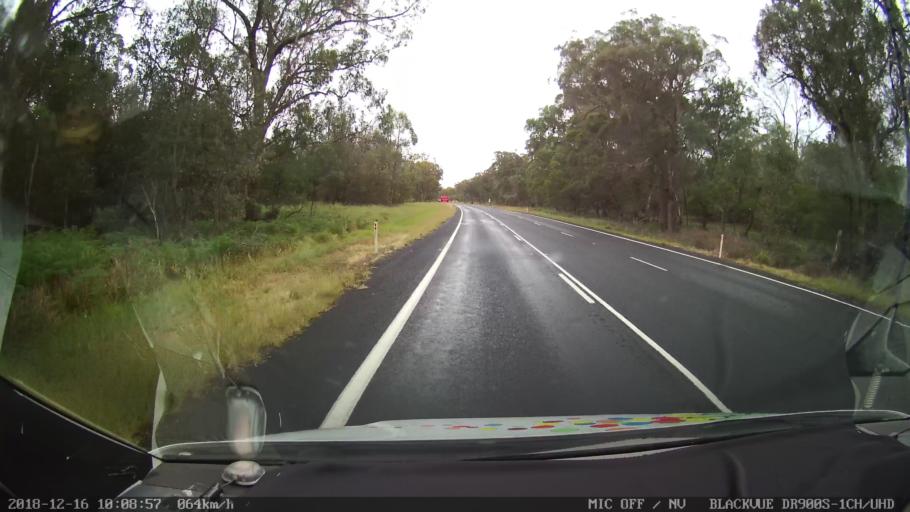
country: AU
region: New South Wales
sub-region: Glen Innes Severn
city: Glen Innes
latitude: -29.3266
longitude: 151.9126
